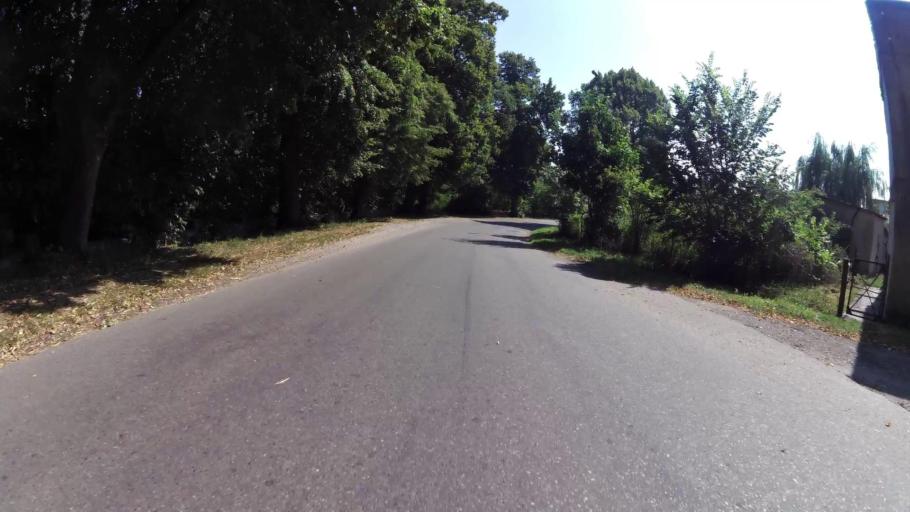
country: PL
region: West Pomeranian Voivodeship
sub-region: Powiat walecki
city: Walcz
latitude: 53.2011
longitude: 16.4939
